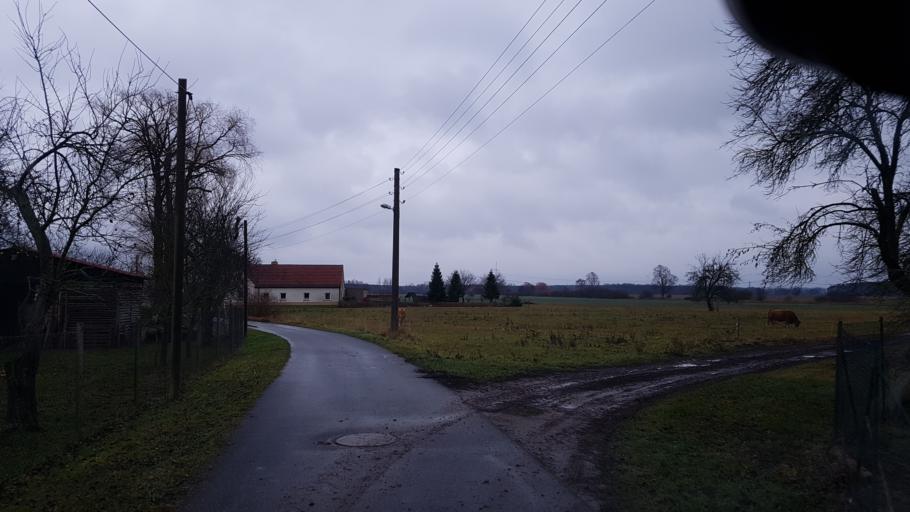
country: DE
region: Brandenburg
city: Sallgast
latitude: 51.6387
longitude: 13.8615
